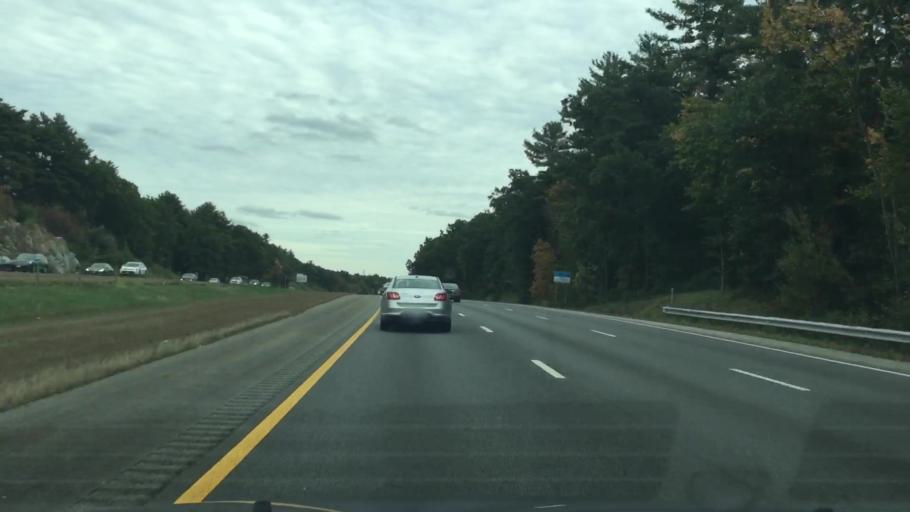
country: US
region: Massachusetts
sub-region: Middlesex County
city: Billerica
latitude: 42.5287
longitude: -71.2728
